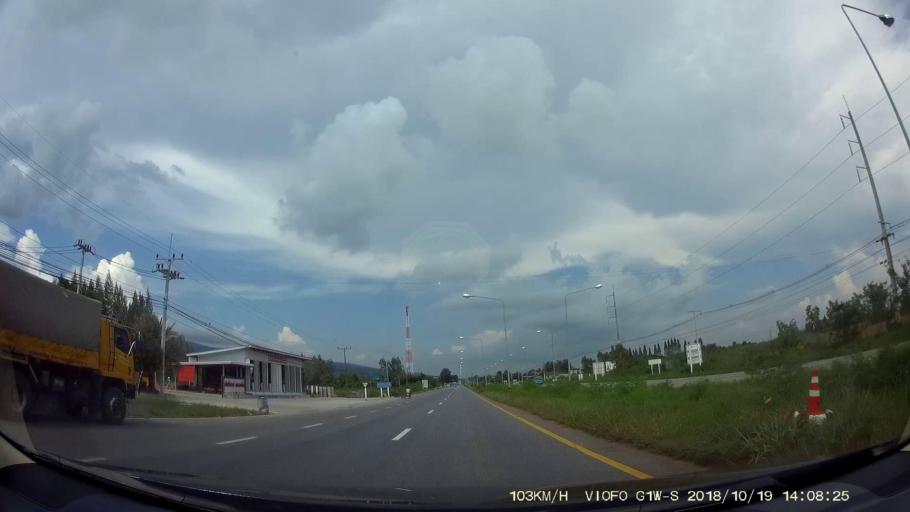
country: TH
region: Chaiyaphum
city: Chaiyaphum
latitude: 15.9063
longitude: 102.1238
